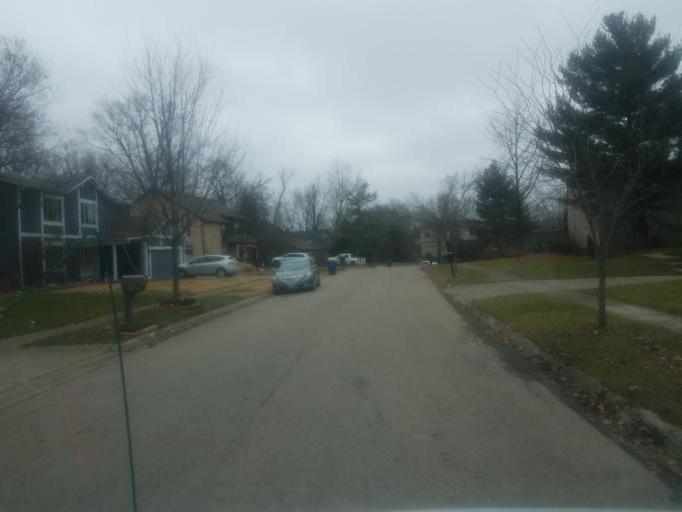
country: US
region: Ohio
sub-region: Franklin County
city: Minerva Park
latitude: 40.0941
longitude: -82.9385
